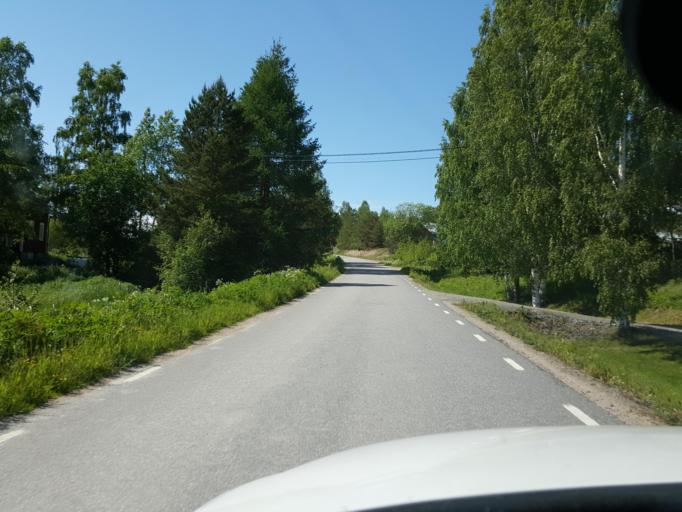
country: SE
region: Gaevleborg
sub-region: Ljusdals Kommun
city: Jaervsoe
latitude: 61.7466
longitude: 16.2663
